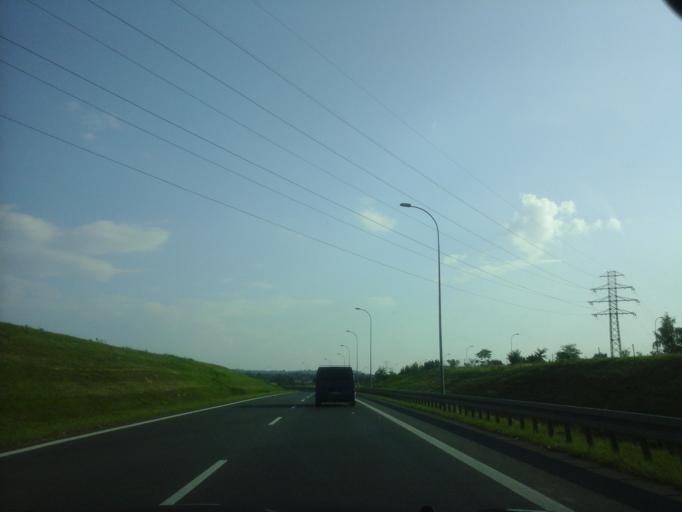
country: PL
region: Lesser Poland Voivodeship
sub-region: Powiat wielicki
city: Czarnochowice
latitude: 50.0146
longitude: 20.0601
